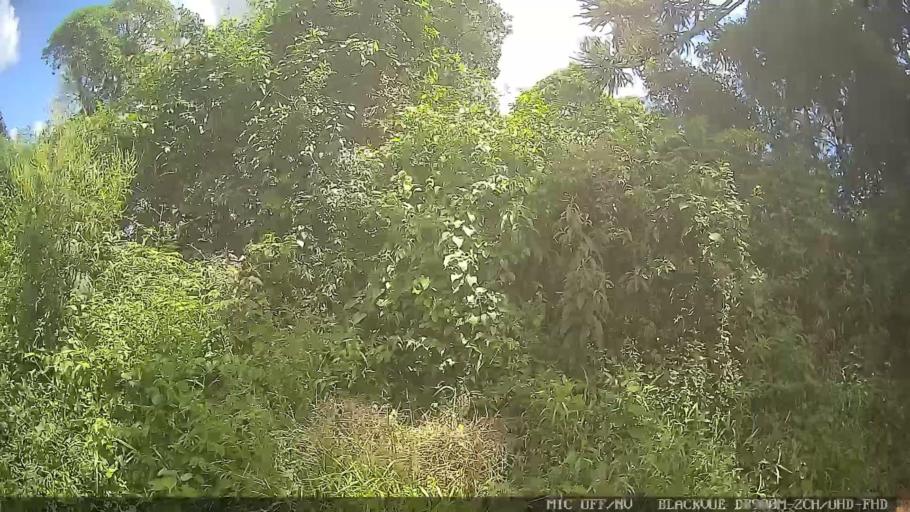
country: BR
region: Minas Gerais
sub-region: Extrema
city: Extrema
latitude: -22.8865
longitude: -46.3086
